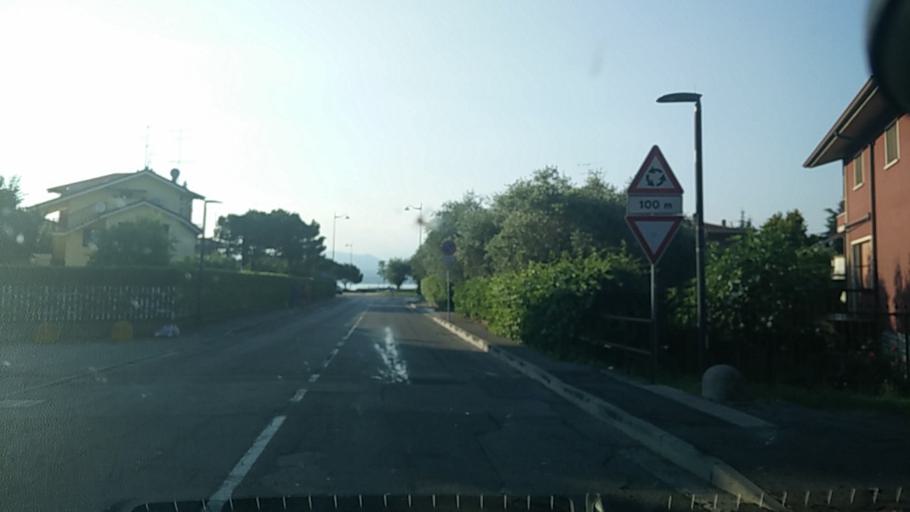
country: IT
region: Lombardy
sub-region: Provincia di Brescia
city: Desenzano del Garda
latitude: 45.4586
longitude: 10.5760
